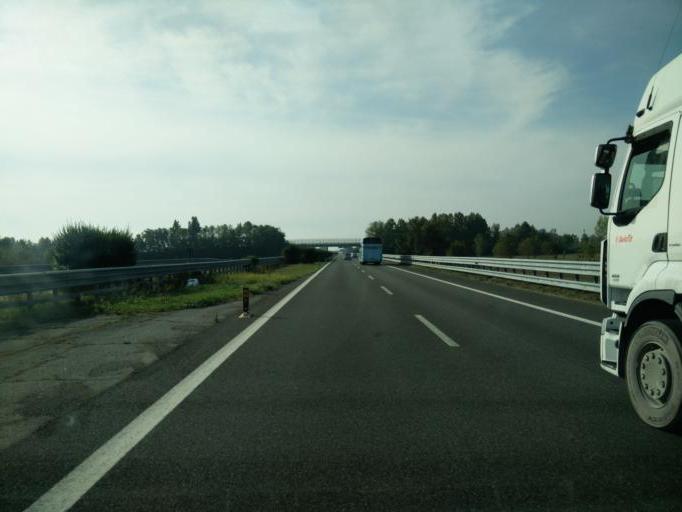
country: IT
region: Lombardy
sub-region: Provincia di Brescia
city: Alfianello
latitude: 45.2851
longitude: 10.1332
